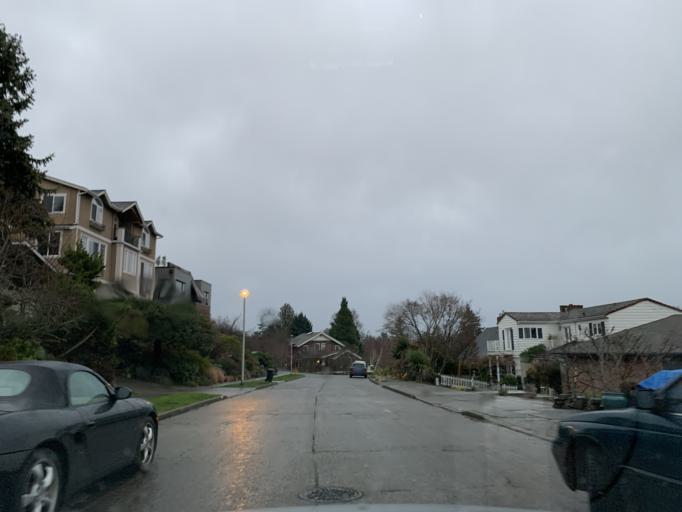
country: US
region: Washington
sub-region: King County
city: Yarrow Point
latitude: 47.6714
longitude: -122.2731
